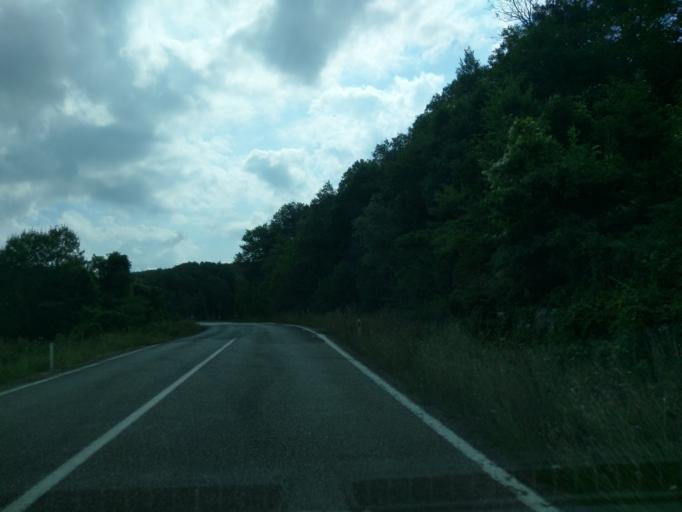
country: TR
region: Sinop
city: Yenikonak
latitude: 41.9463
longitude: 34.7475
